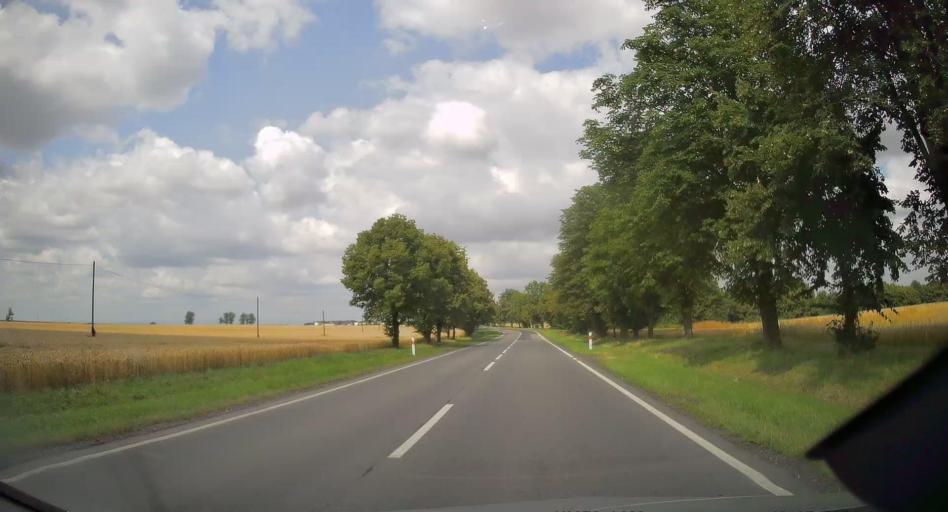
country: PL
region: Opole Voivodeship
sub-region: Powiat prudnicki
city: Twardawa
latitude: 50.3417
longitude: 18.0130
